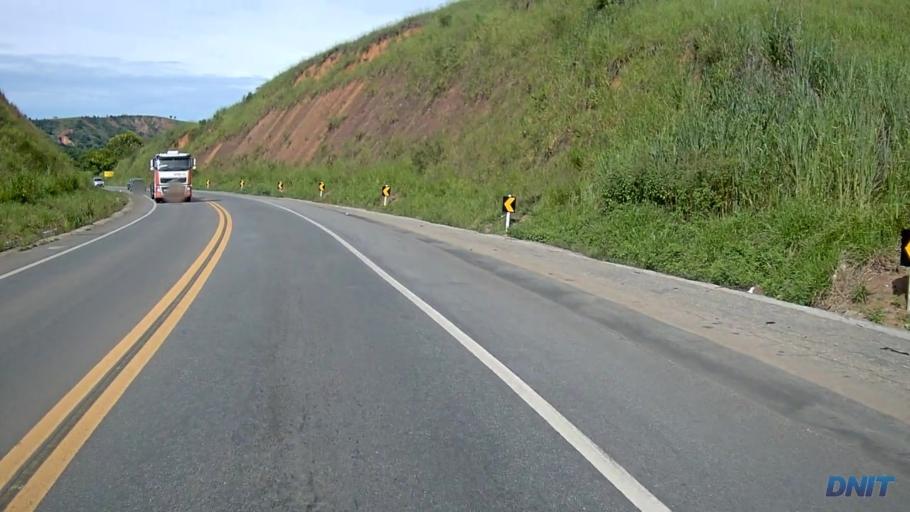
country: BR
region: Minas Gerais
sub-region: Belo Oriente
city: Belo Oriente
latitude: -19.2647
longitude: -42.3472
